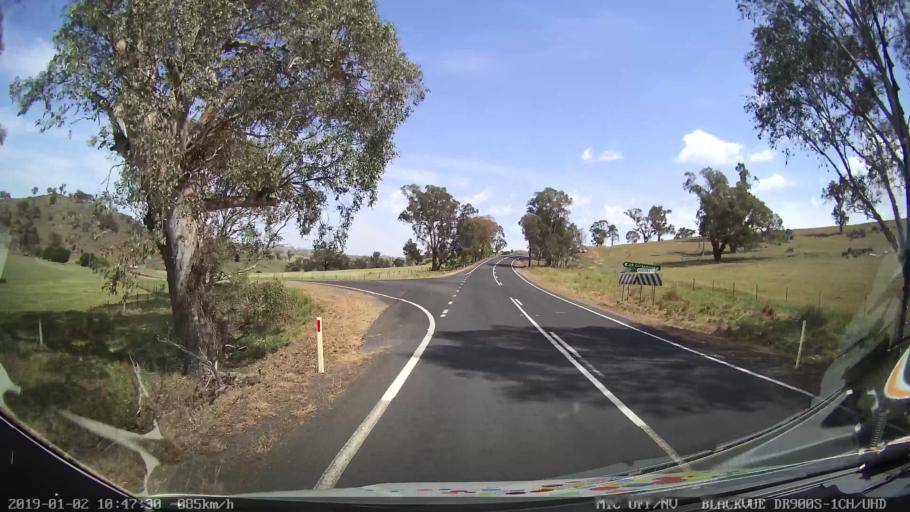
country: AU
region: New South Wales
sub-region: Cootamundra
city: Cootamundra
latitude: -34.7445
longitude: 148.2730
